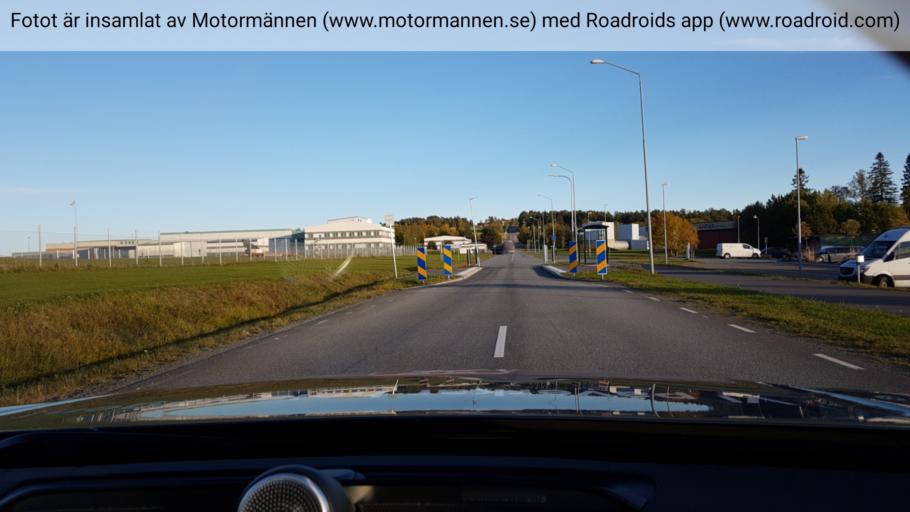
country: SE
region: Jaemtland
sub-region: Krokoms Kommun
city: Krokom
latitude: 63.1931
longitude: 14.4879
